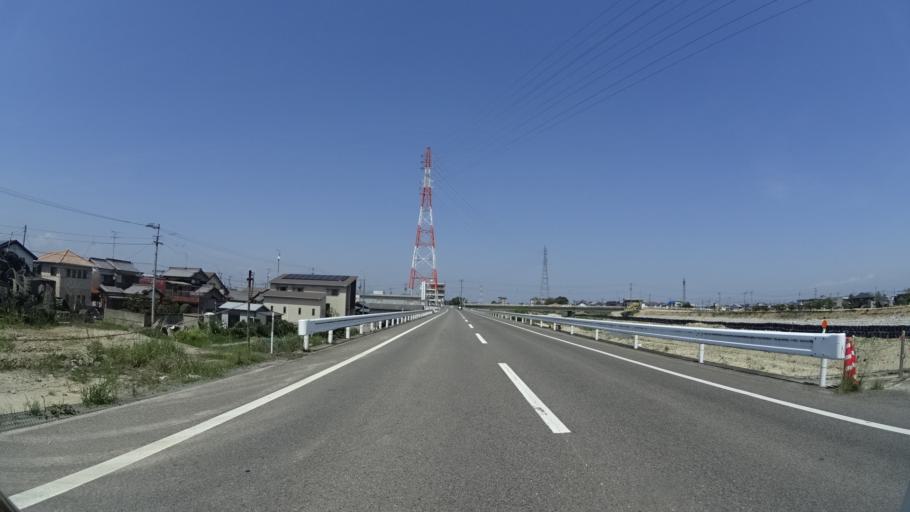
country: JP
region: Ehime
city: Hojo
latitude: 34.0375
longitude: 132.9752
